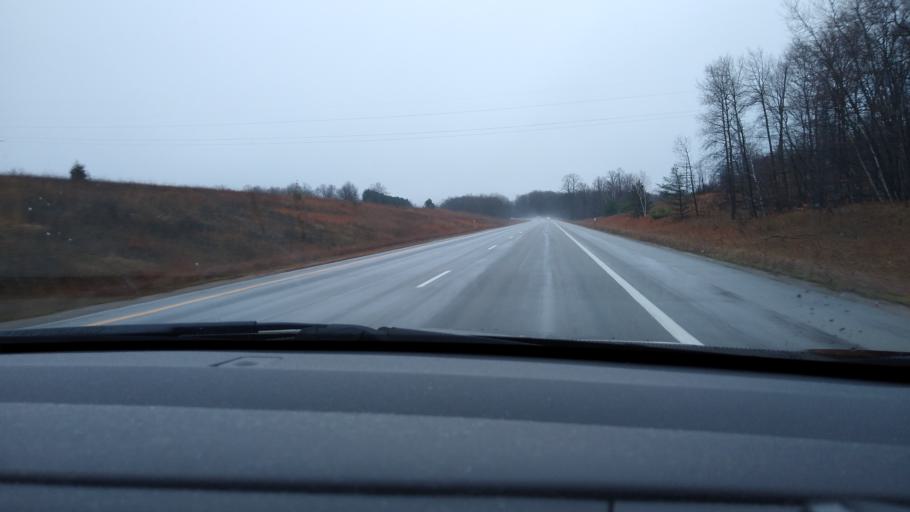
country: US
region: Michigan
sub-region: Cheboygan County
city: Indian River
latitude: 45.3312
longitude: -84.6056
